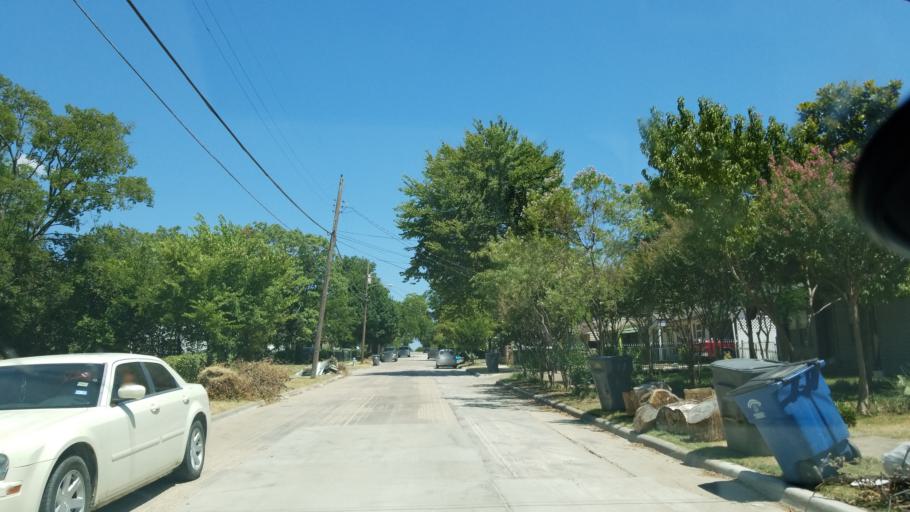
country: US
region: Texas
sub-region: Dallas County
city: Cockrell Hill
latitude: 32.7265
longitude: -96.8906
